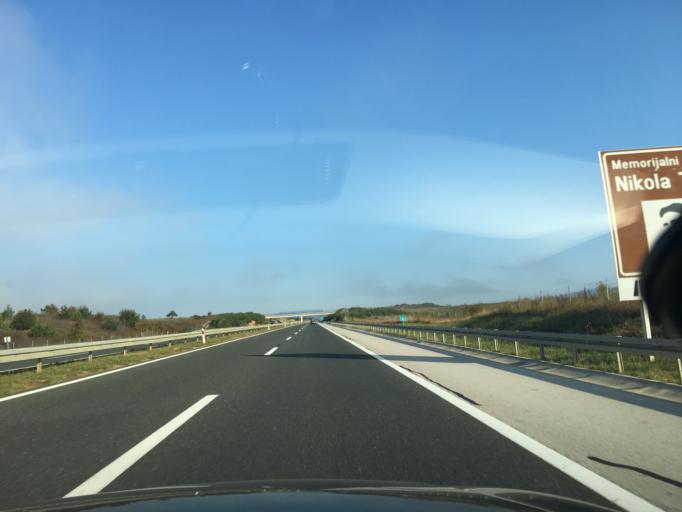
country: HR
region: Licko-Senjska
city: Gospic
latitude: 44.5504
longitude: 15.4332
